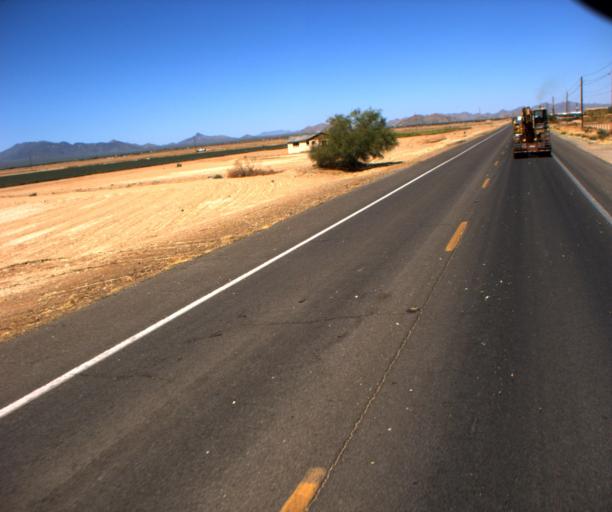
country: US
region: Arizona
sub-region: Pinal County
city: Maricopa
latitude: 32.8794
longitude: -112.0027
